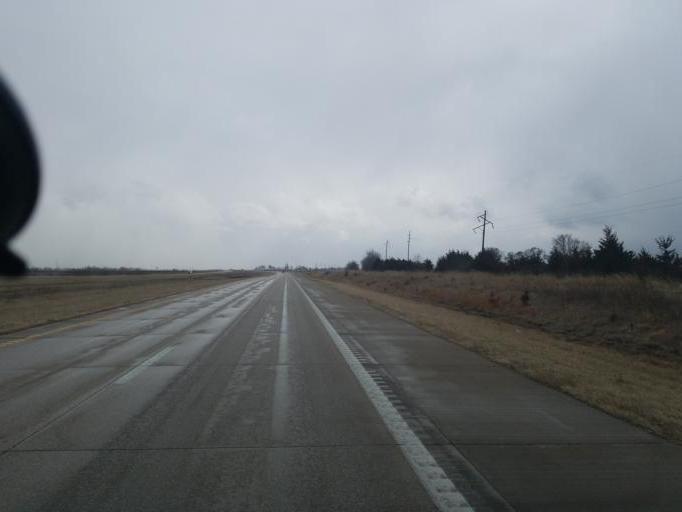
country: US
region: Missouri
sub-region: Randolph County
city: Moberly
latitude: 39.5363
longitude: -92.4476
